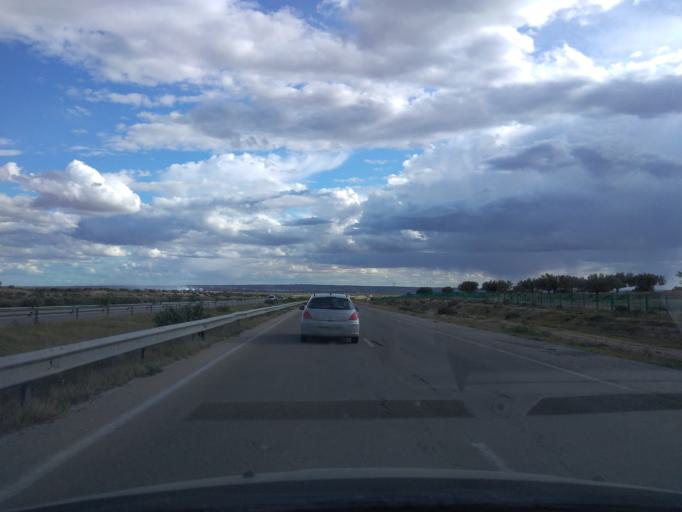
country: TN
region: Al Munastir
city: Manzil Kamil
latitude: 35.5314
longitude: 10.6252
